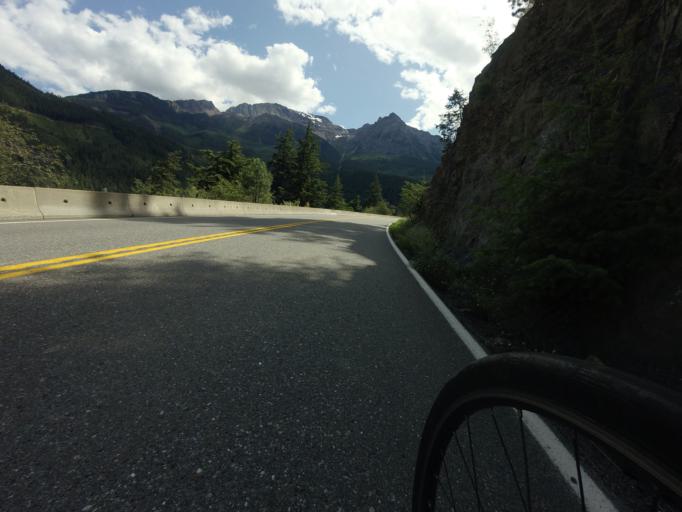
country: CA
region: British Columbia
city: Lillooet
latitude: 50.6540
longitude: -122.0018
